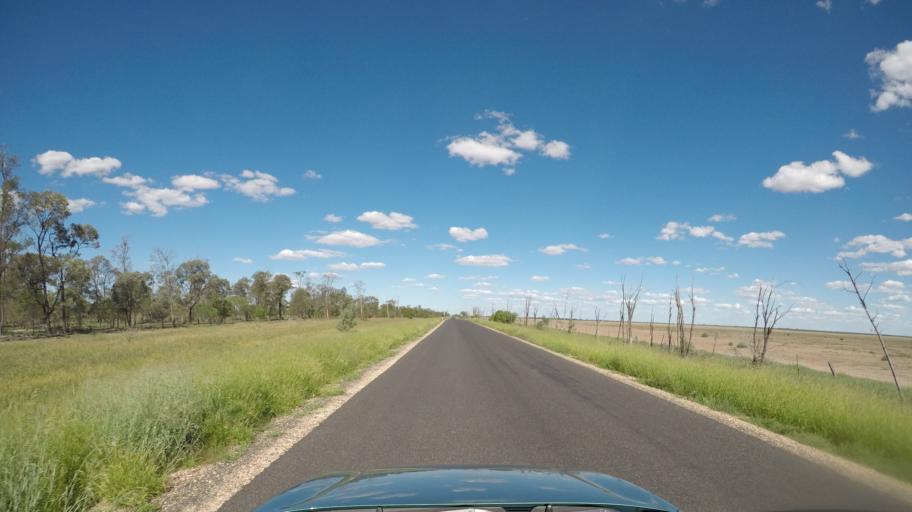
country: AU
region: Queensland
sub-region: Goondiwindi
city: Goondiwindi
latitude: -28.1621
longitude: 150.1459
